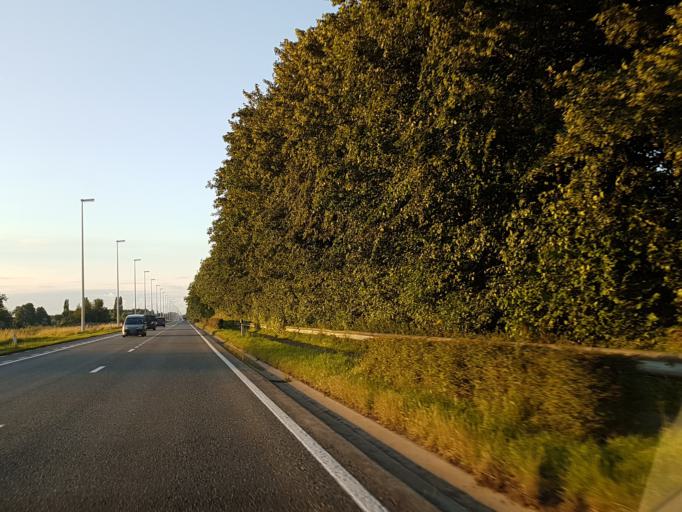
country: BE
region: Flanders
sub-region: Provincie Oost-Vlaanderen
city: Dendermonde
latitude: 51.0484
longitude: 4.1216
